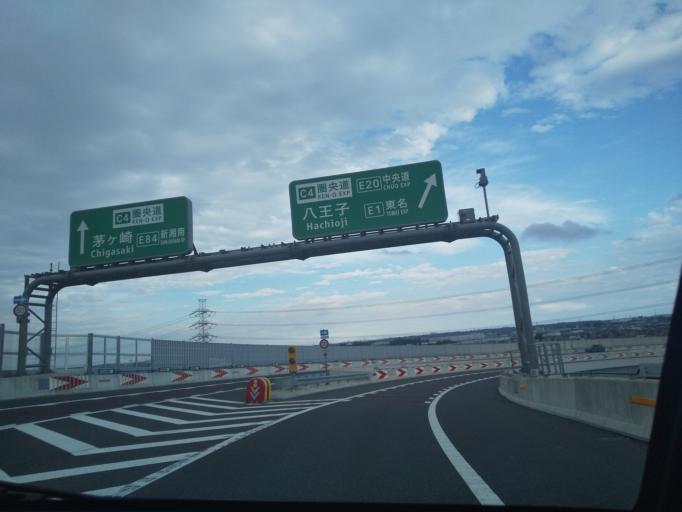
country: JP
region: Kanagawa
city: Atsugi
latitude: 35.4097
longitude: 139.3743
